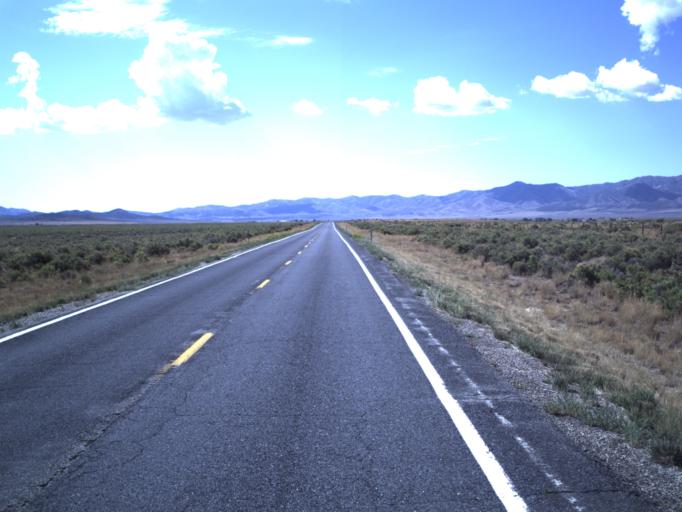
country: US
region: Utah
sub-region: Tooele County
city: Tooele
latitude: 40.1425
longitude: -112.4308
